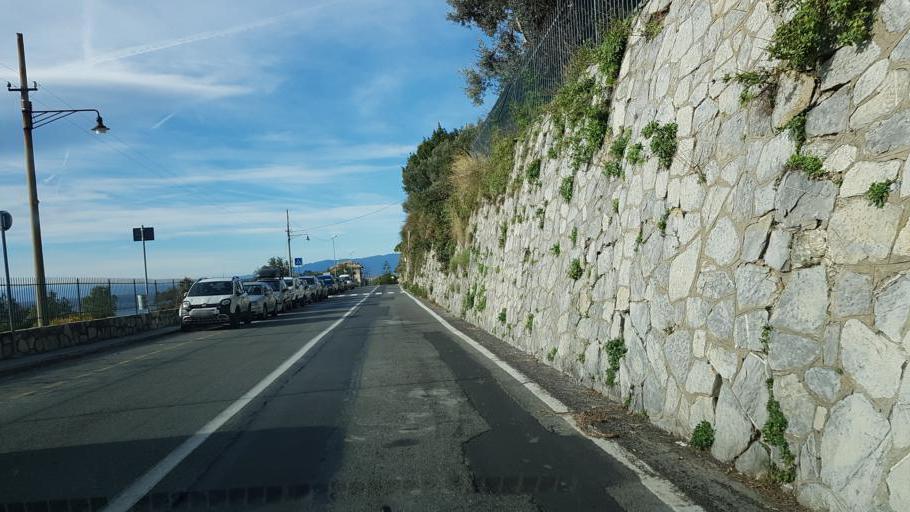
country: IT
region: Liguria
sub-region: Provincia di Genova
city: Sori
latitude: 44.3680
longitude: 9.1140
